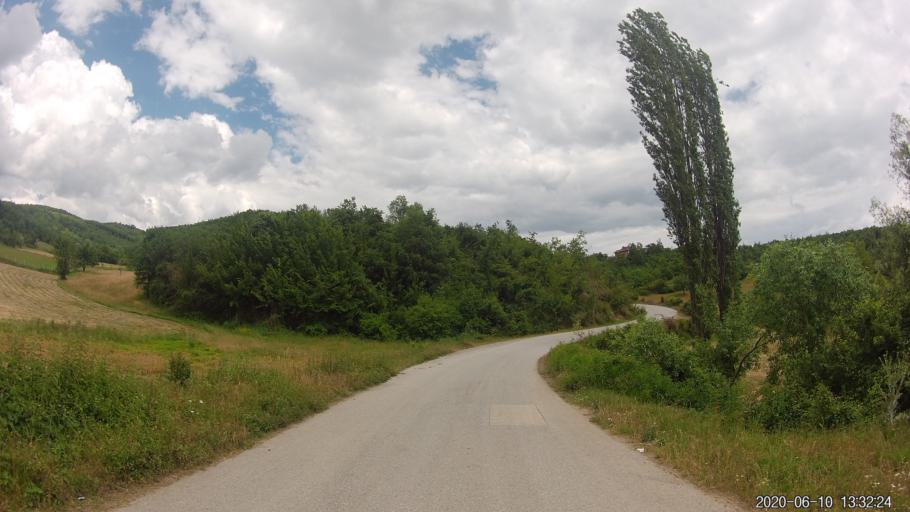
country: XK
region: Prizren
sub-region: Komuna e Therandes
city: Peqan
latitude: 42.4110
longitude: 20.8810
